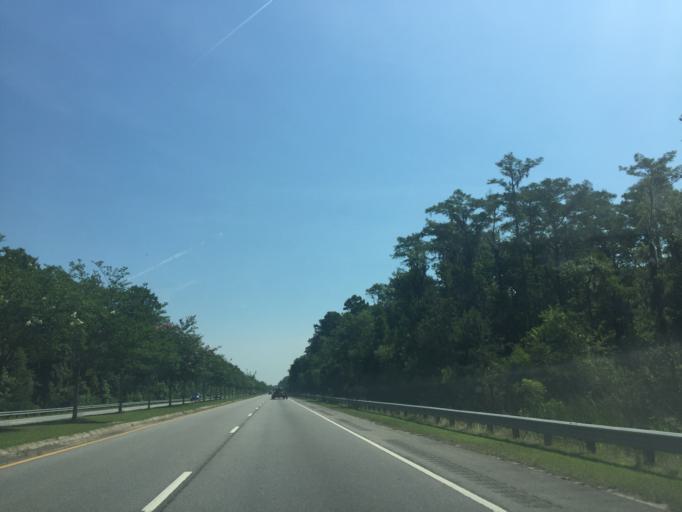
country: US
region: Georgia
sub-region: Bryan County
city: Richmond Hill
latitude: 31.9638
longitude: -81.3012
